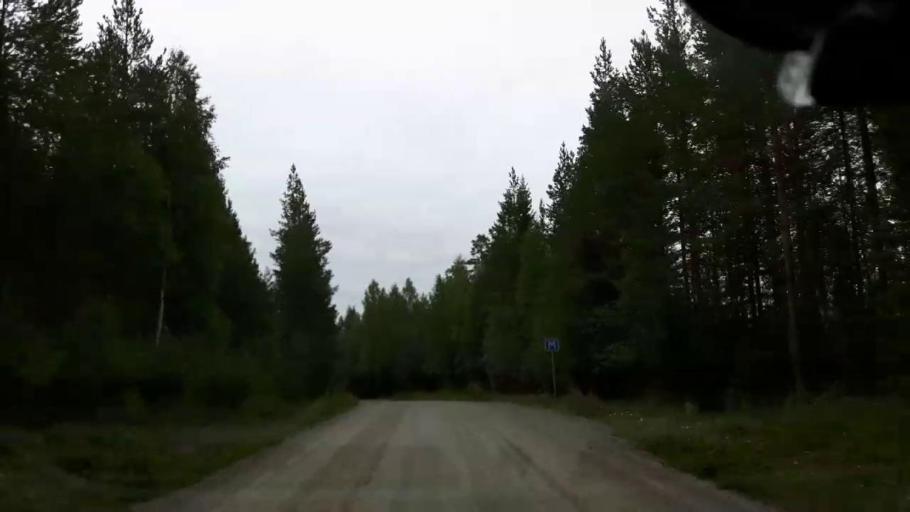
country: SE
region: Jaemtland
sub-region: Braecke Kommun
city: Braecke
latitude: 62.8286
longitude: 15.6952
